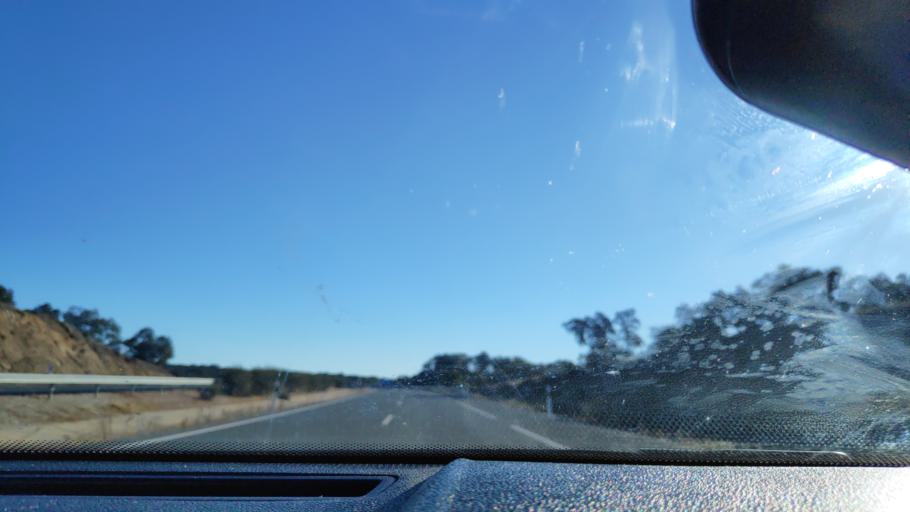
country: ES
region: Andalusia
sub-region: Provincia de Huelva
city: Santa Olalla del Cala
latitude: 37.9294
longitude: -6.2280
